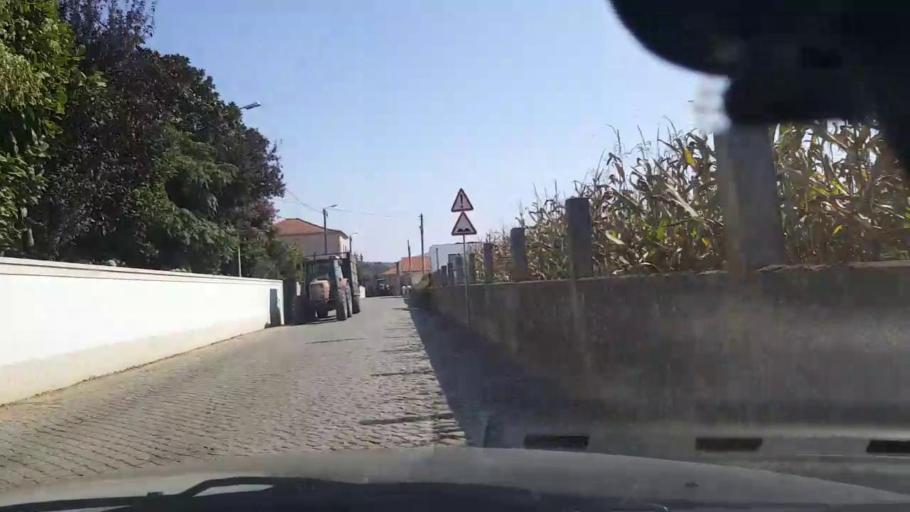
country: PT
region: Porto
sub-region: Povoa de Varzim
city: Pedroso
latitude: 41.4113
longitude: -8.6962
